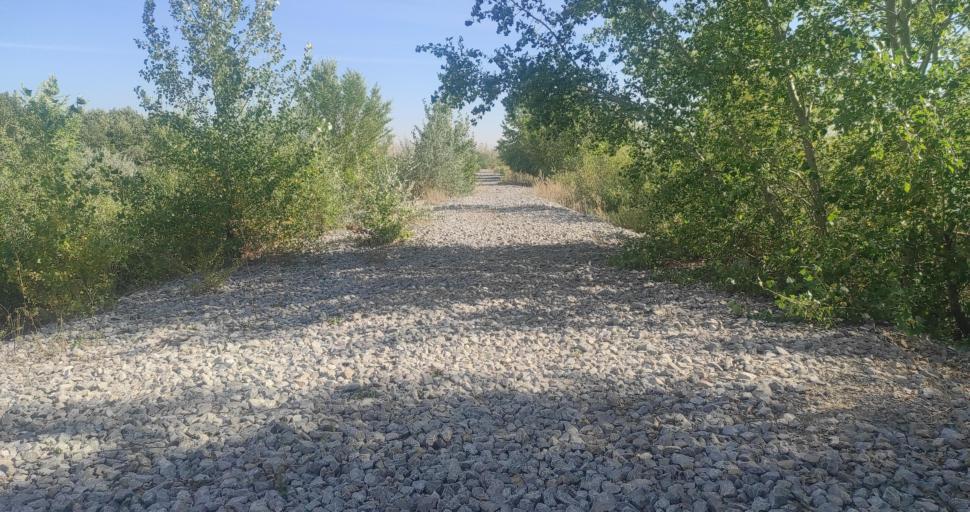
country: RU
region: Bashkortostan
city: Sibay
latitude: 52.7529
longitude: 58.6832
